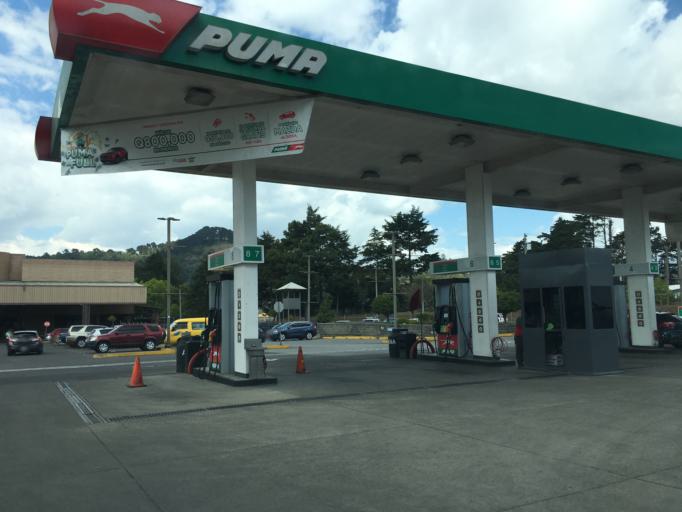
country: GT
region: Guatemala
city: Santa Catarina Pinula
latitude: 14.5550
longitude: -90.4551
